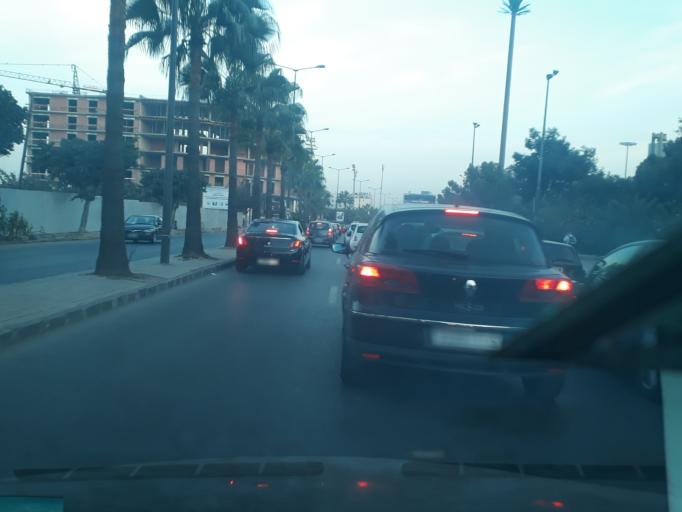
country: MA
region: Grand Casablanca
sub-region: Casablanca
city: Casablanca
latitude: 33.5799
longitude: -7.6468
